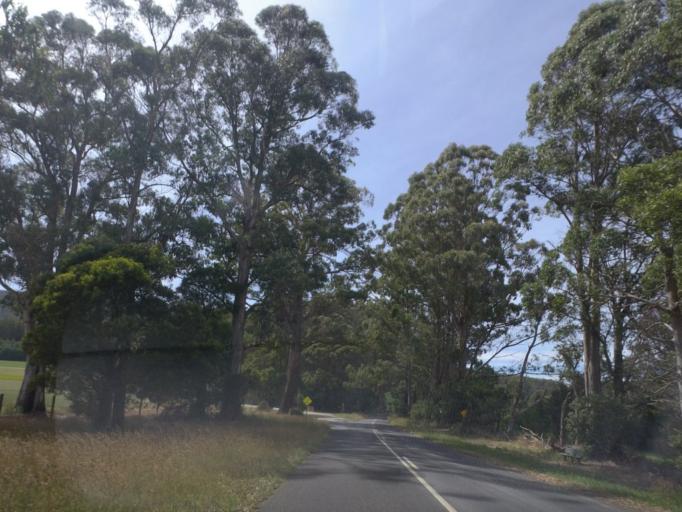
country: AU
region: Victoria
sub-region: Yarra Ranges
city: Healesville
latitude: -37.5556
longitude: 145.5022
